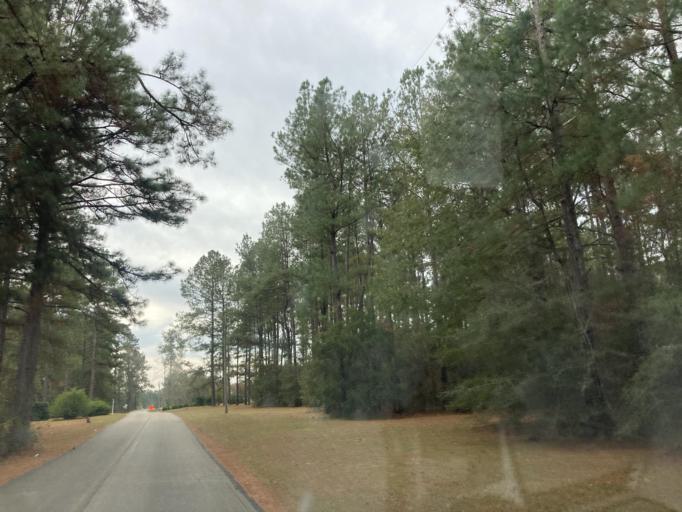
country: US
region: Mississippi
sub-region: Lamar County
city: Purvis
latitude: 31.1426
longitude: -89.4609
